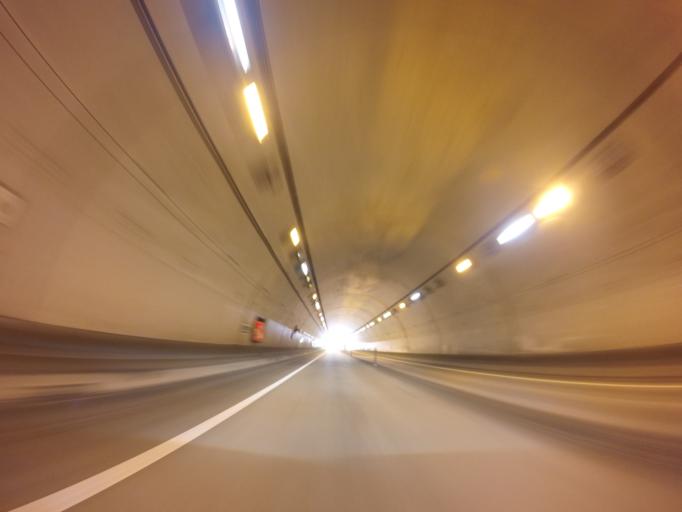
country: JP
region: Shizuoka
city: Mishima
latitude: 34.9721
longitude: 138.9372
